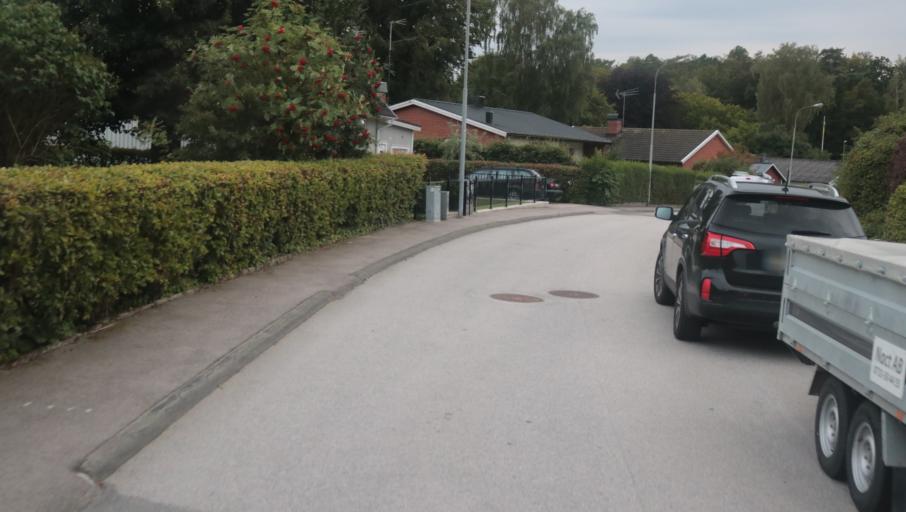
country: SE
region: Blekinge
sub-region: Karlshamns Kommun
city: Karlshamn
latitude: 56.1634
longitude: 14.8846
